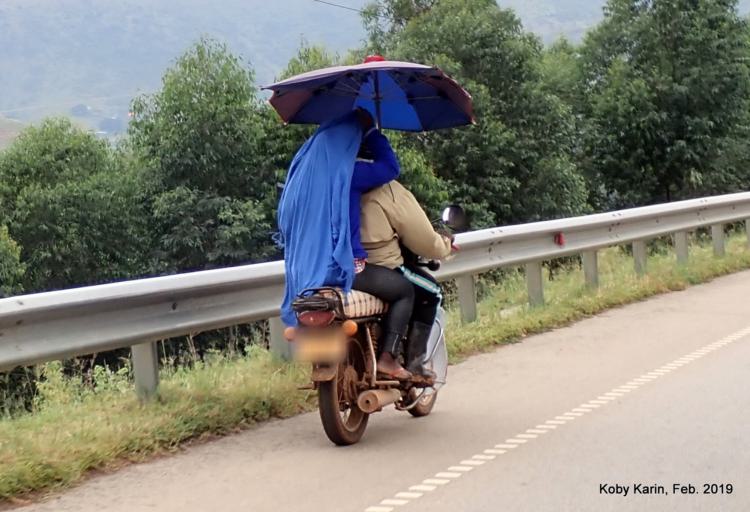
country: UG
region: Western Region
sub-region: Kabale District
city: Kabale
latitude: -1.1231
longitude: 30.1779
